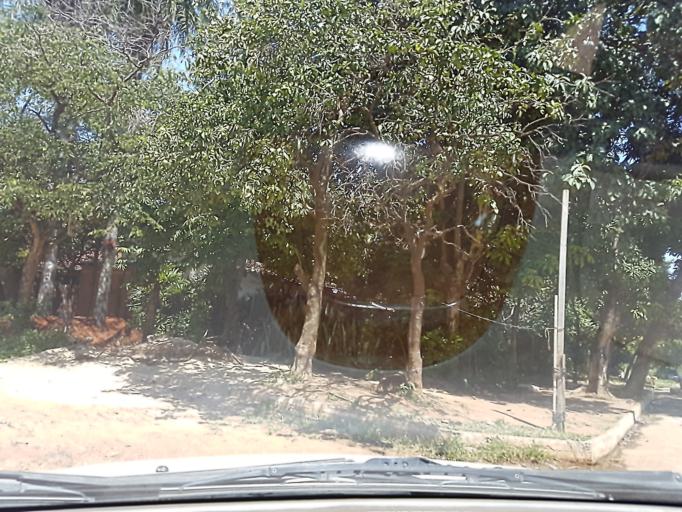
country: PY
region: Central
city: Fernando de la Mora
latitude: -25.2922
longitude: -57.5339
